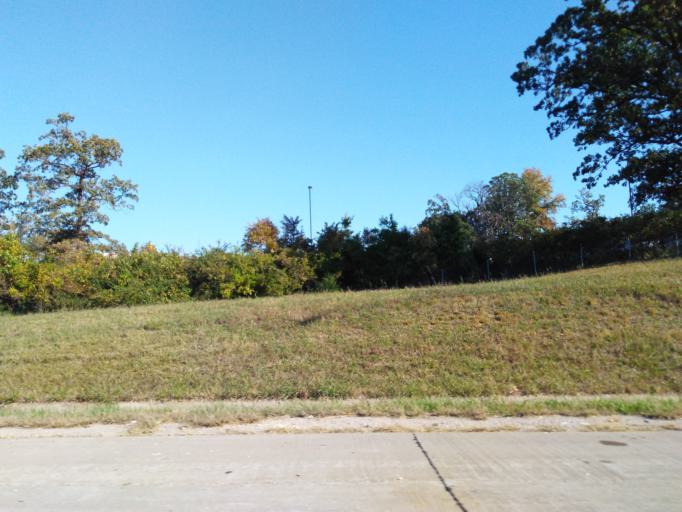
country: US
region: Missouri
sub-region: Saint Louis County
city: Oakville
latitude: 38.4885
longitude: -90.2810
